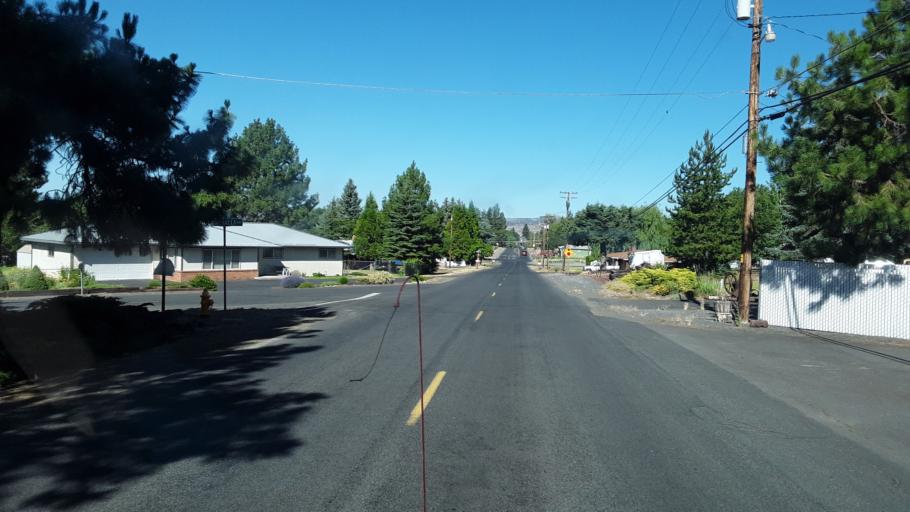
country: US
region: Oregon
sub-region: Klamath County
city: Altamont
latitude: 42.2139
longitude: -121.7101
